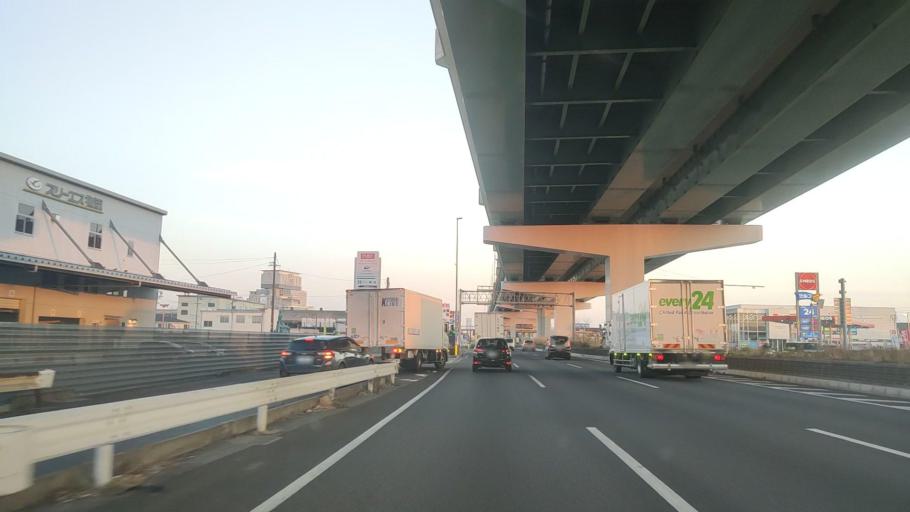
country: JP
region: Aichi
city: Iwakura
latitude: 35.2683
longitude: 136.8345
